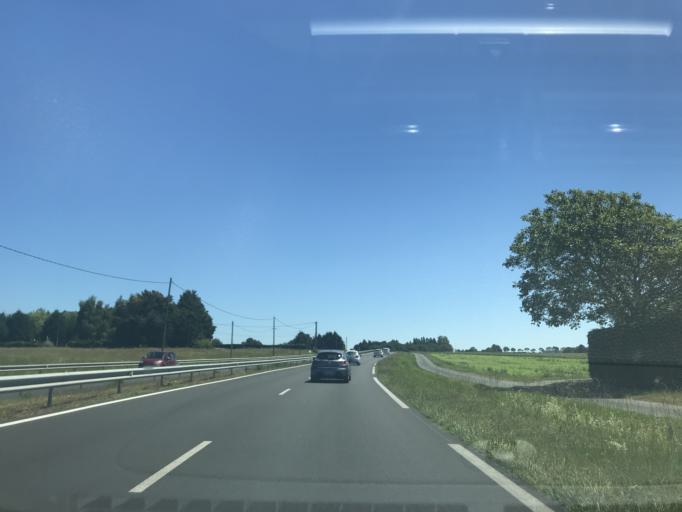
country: FR
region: Poitou-Charentes
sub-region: Departement de la Charente-Maritime
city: Vaux-sur-Mer
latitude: 45.6556
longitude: -1.0546
